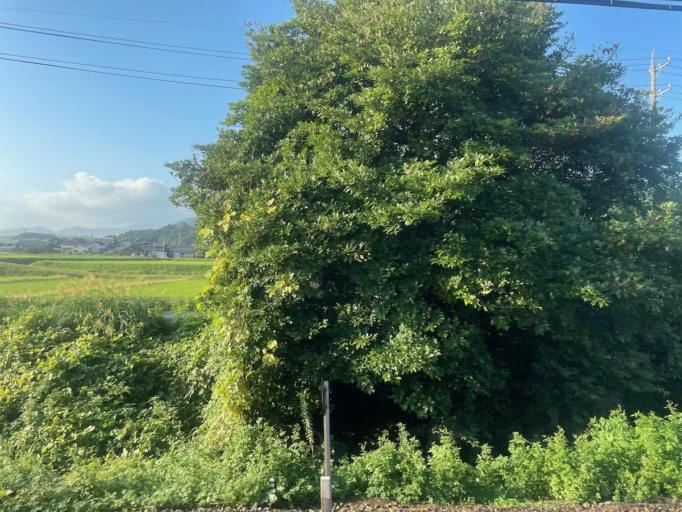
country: JP
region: Mie
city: Hisai-motomachi
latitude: 34.6542
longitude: 136.4435
